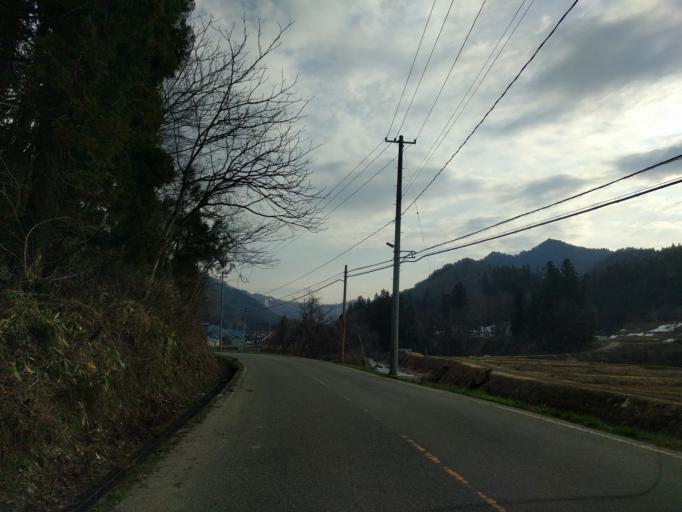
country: JP
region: Fukushima
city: Kitakata
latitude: 37.7100
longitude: 139.9186
